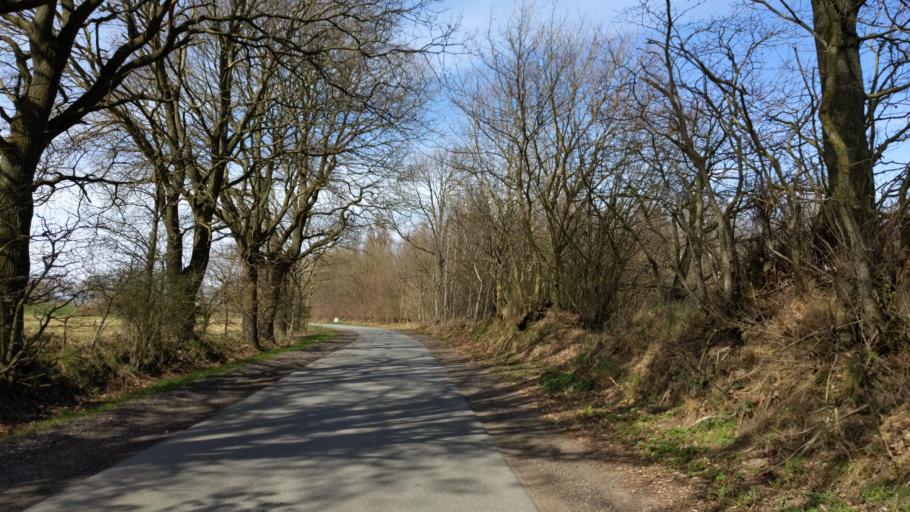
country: DE
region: Schleswig-Holstein
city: Ratekau
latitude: 53.9744
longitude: 10.6925
